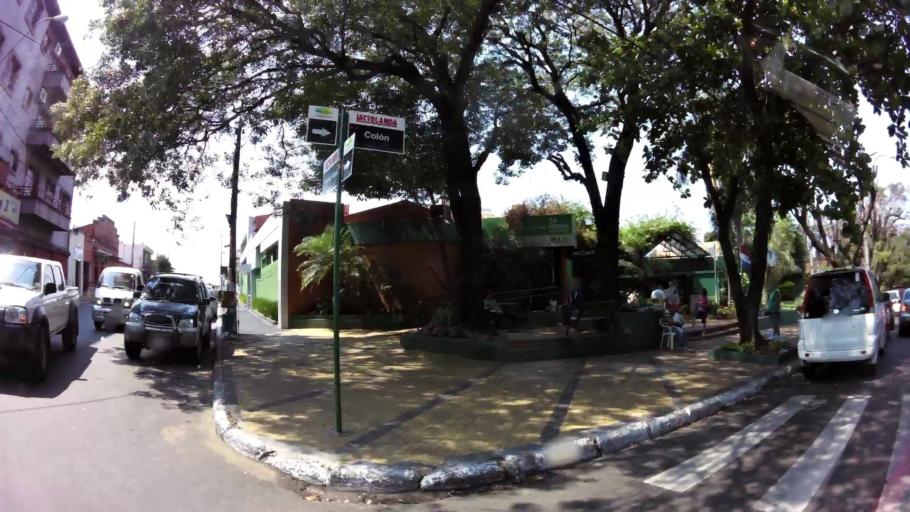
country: PY
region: Asuncion
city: Asuncion
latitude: -25.2903
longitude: -57.6497
